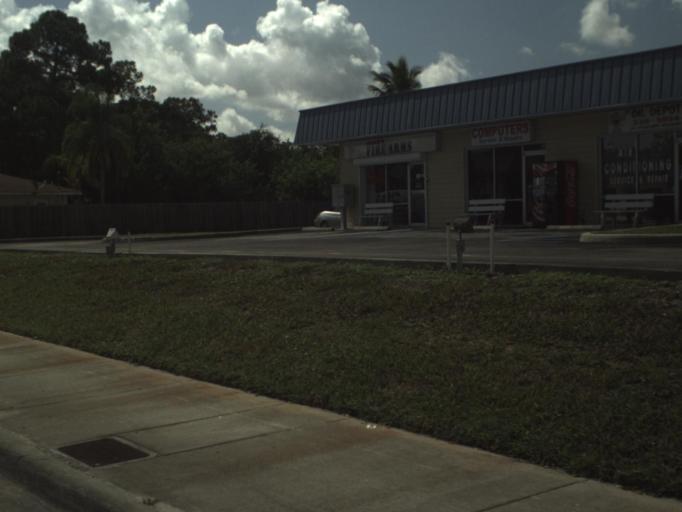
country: US
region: Florida
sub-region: Saint Lucie County
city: Port Saint Lucie
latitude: 27.2736
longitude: -80.3472
